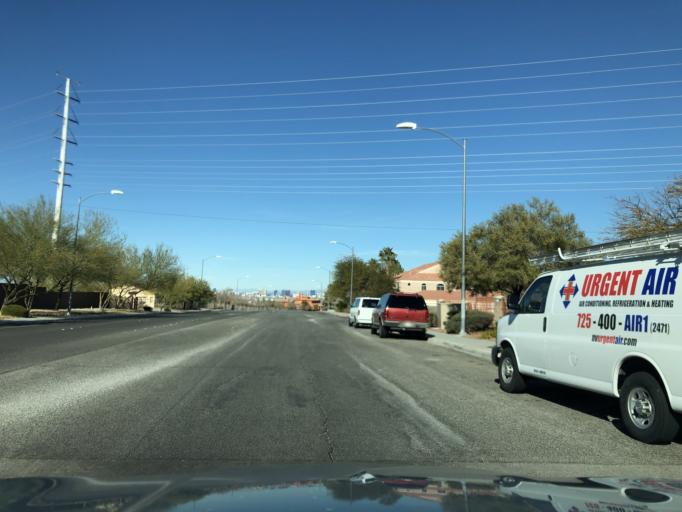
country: US
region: Nevada
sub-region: Clark County
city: Whitney
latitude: 36.0017
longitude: -115.0944
